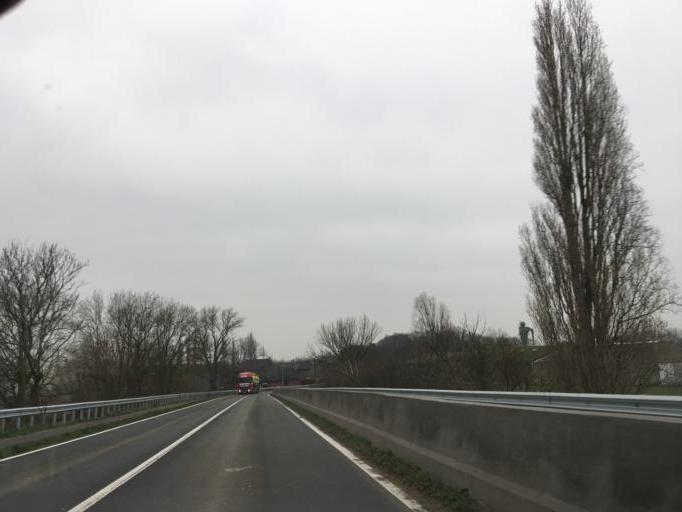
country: BE
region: Flanders
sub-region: Provincie West-Vlaanderen
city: Oostrozebeke
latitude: 50.9075
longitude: 3.3255
